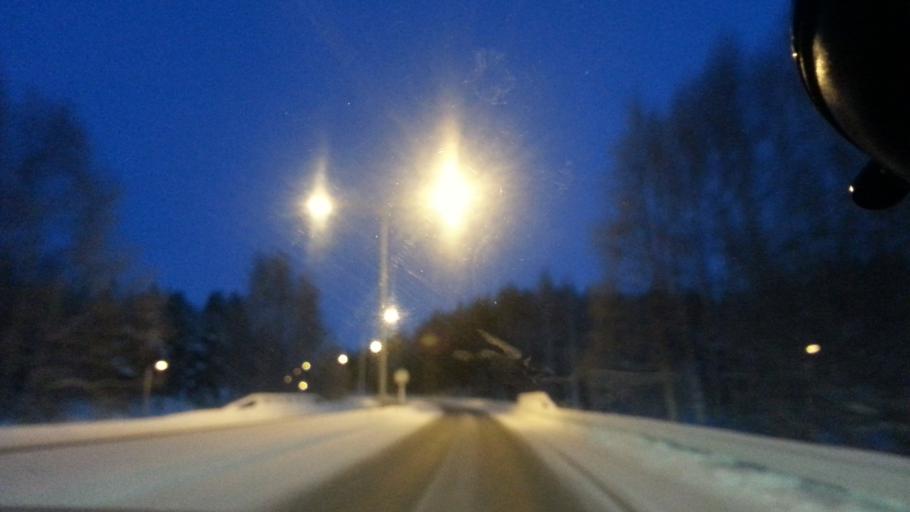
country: FI
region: Lapland
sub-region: Rovaniemi
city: Rovaniemi
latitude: 66.4915
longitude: 25.7570
